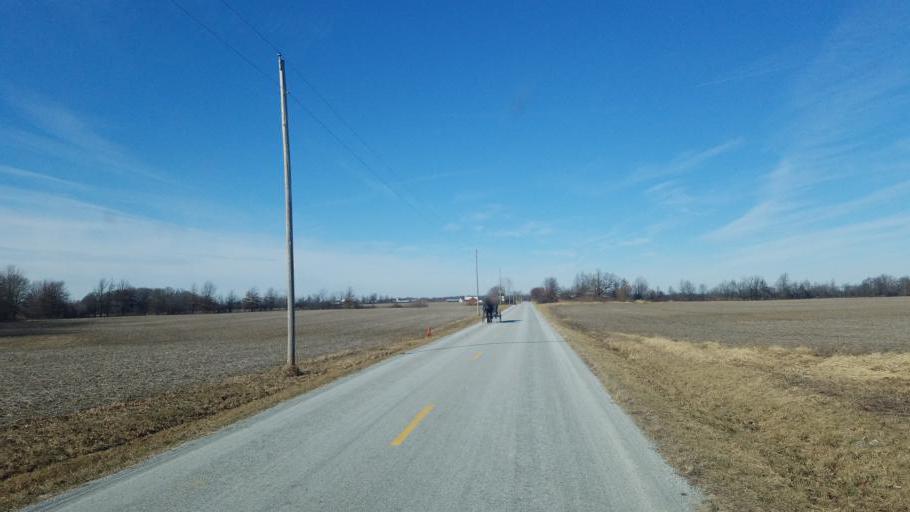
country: US
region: Ohio
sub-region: Hardin County
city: Kenton
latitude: 40.5721
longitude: -83.4291
